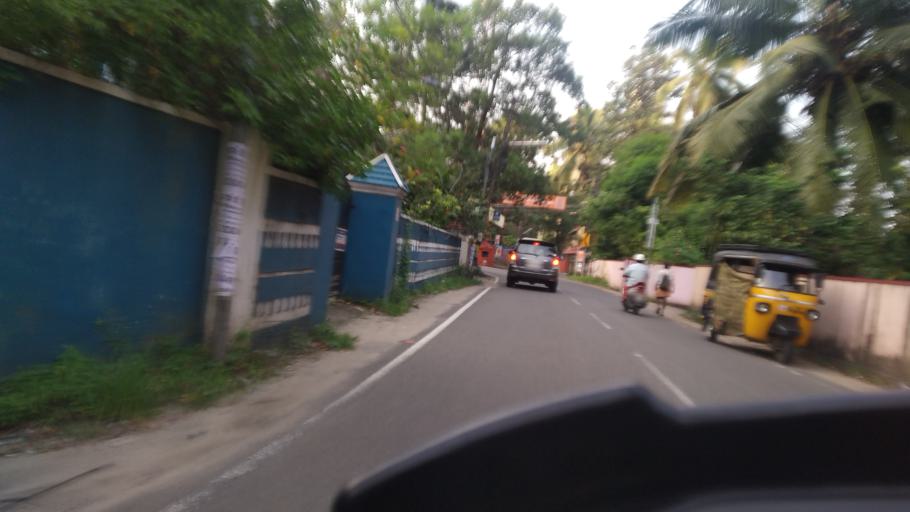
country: IN
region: Kerala
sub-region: Ernakulam
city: Elur
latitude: 10.0234
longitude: 76.3001
